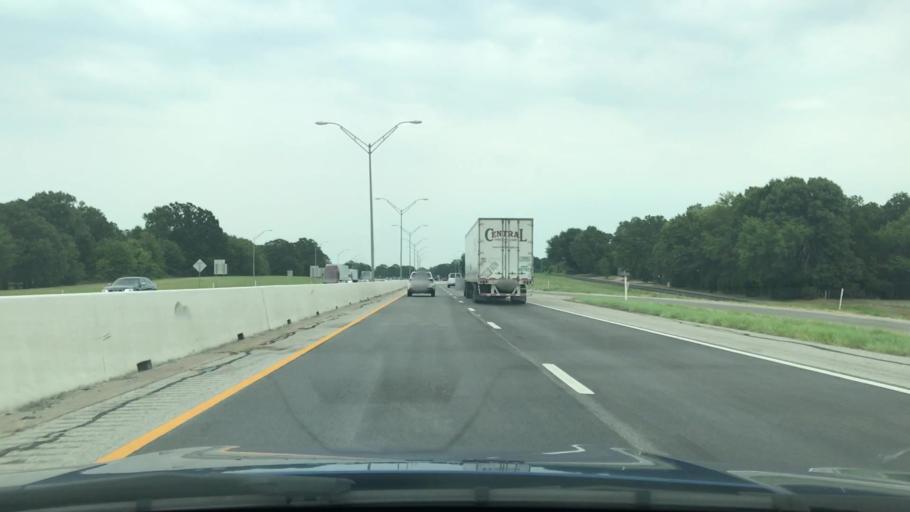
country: US
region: Texas
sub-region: Van Zandt County
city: Van
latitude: 32.5178
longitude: -95.6947
